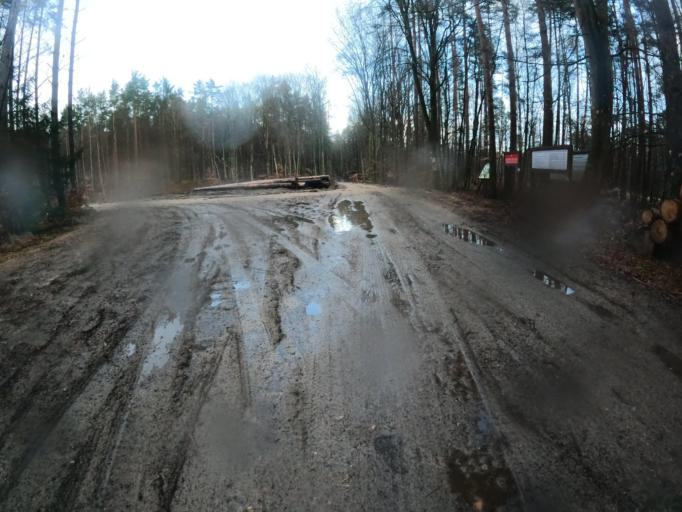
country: PL
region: West Pomeranian Voivodeship
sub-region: Powiat slawienski
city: Slawno
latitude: 54.2627
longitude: 16.7112
